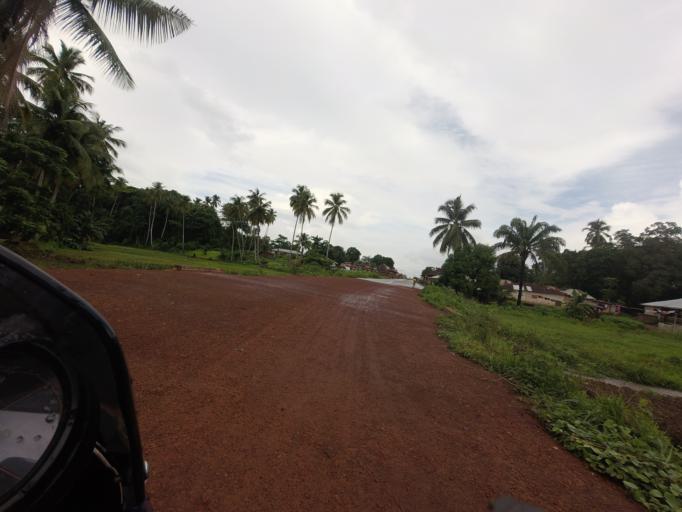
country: SL
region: Northern Province
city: Kambia
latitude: 9.1305
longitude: -12.9184
